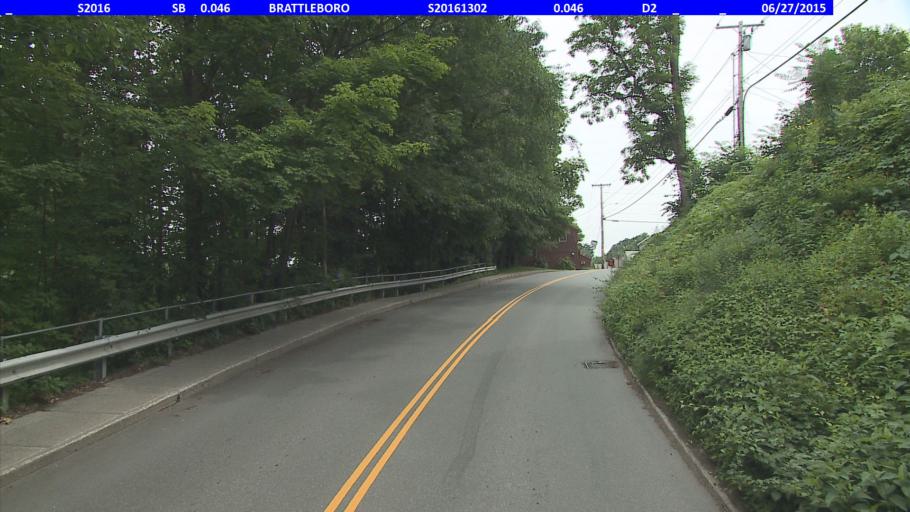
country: US
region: Vermont
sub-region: Windham County
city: Brattleboro
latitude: 42.8492
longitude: -72.5677
